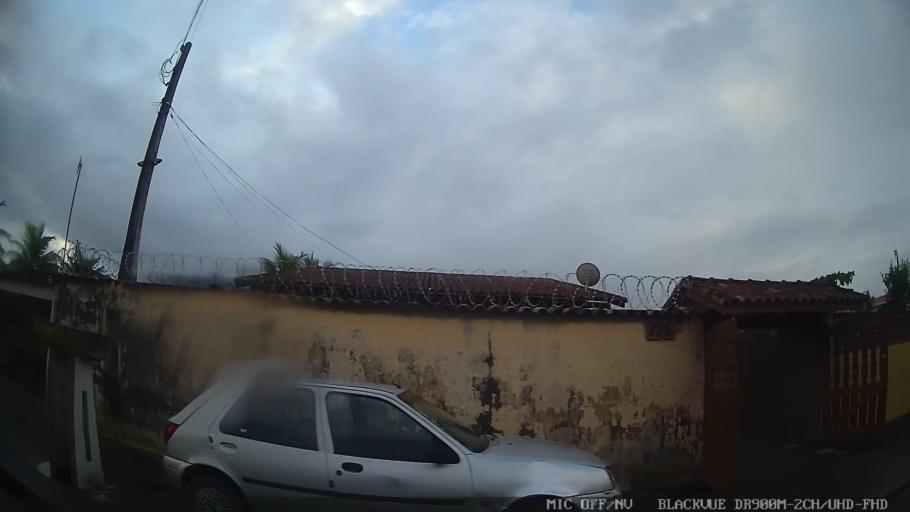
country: BR
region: Sao Paulo
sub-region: Itanhaem
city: Itanhaem
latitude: -24.2012
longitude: -46.8345
